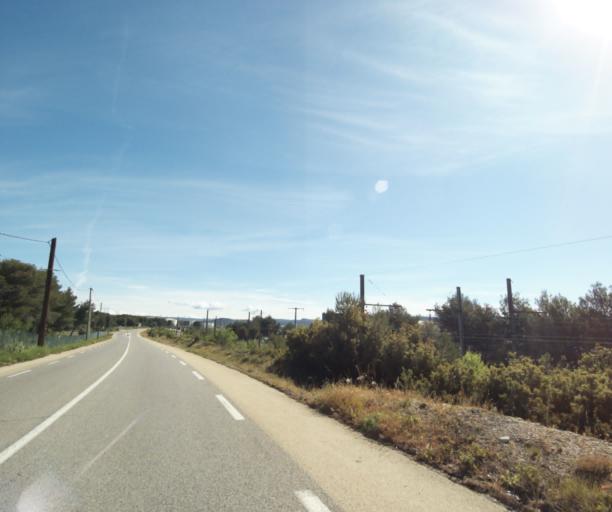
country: FR
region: Provence-Alpes-Cote d'Azur
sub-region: Departement des Bouches-du-Rhone
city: Rognac
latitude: 43.4975
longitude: 5.2064
